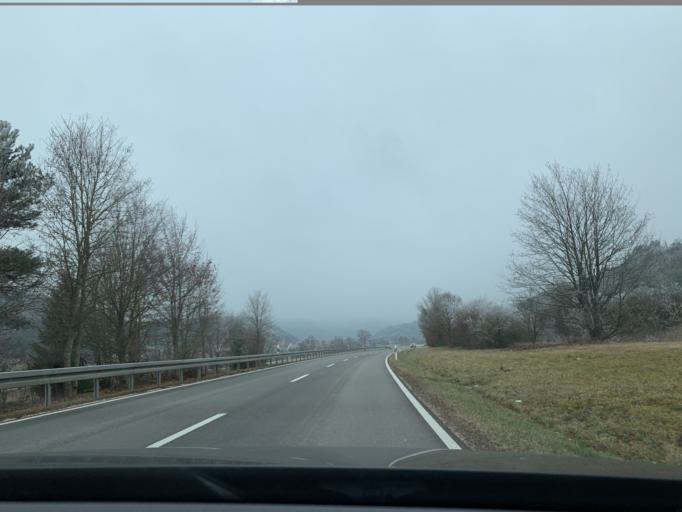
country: DE
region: Baden-Wuerttemberg
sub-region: Freiburg Region
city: Geisingen
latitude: 47.8987
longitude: 8.6687
